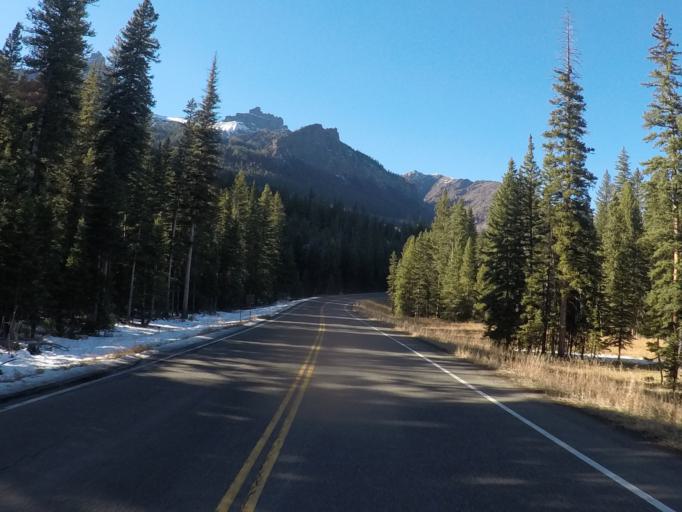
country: US
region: Montana
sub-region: Carbon County
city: Red Lodge
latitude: 44.9758
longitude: -109.8363
